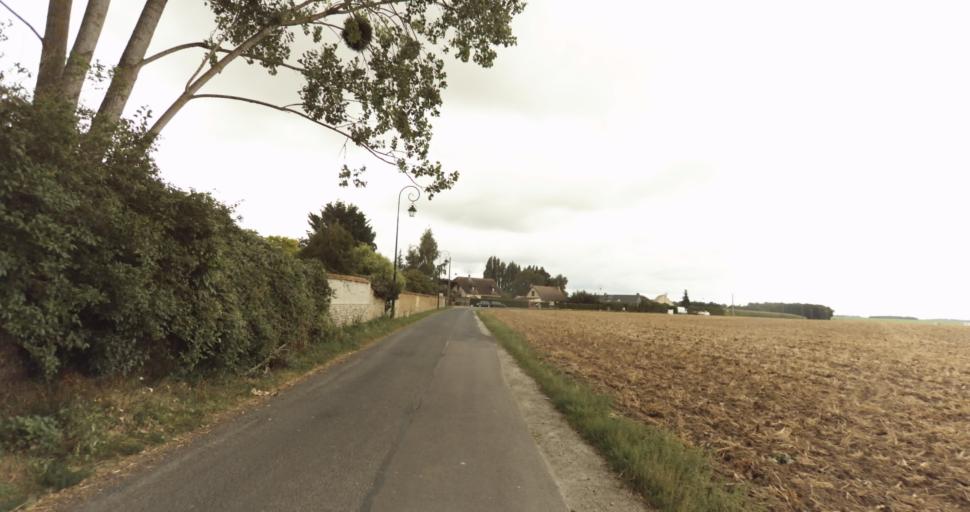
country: FR
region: Haute-Normandie
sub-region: Departement de l'Eure
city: Menilles
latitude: 49.0077
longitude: 1.2779
